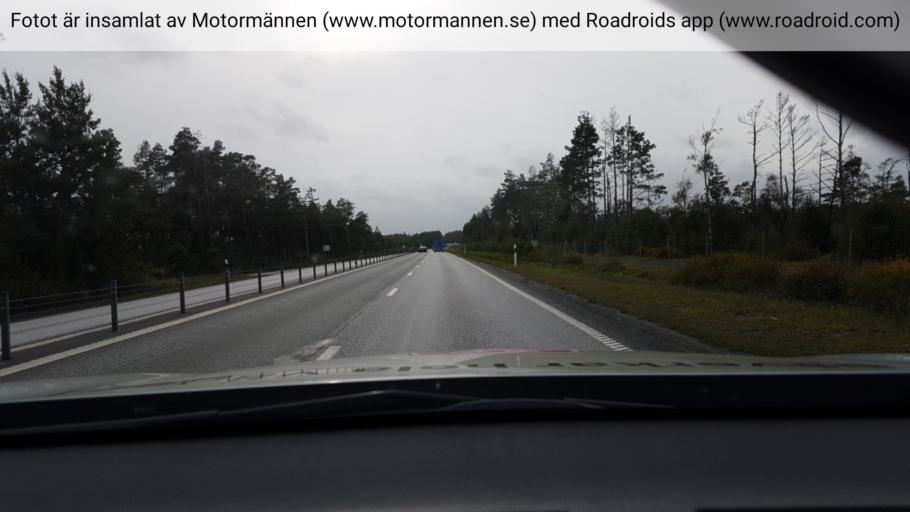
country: SE
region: Joenkoeping
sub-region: Jonkopings Kommun
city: Taberg
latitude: 57.7674
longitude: 14.0283
